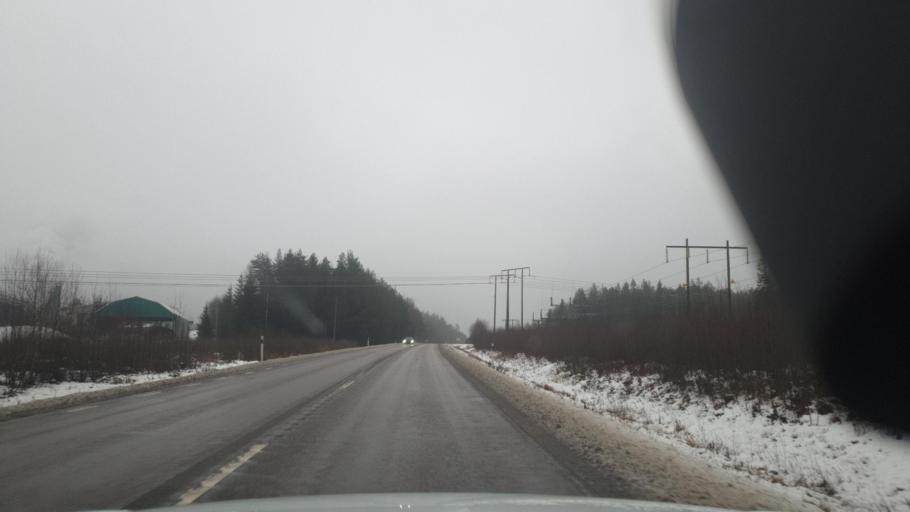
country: SE
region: Vaermland
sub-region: Karlstads Kommun
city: Edsvalla
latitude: 59.4153
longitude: 13.1857
